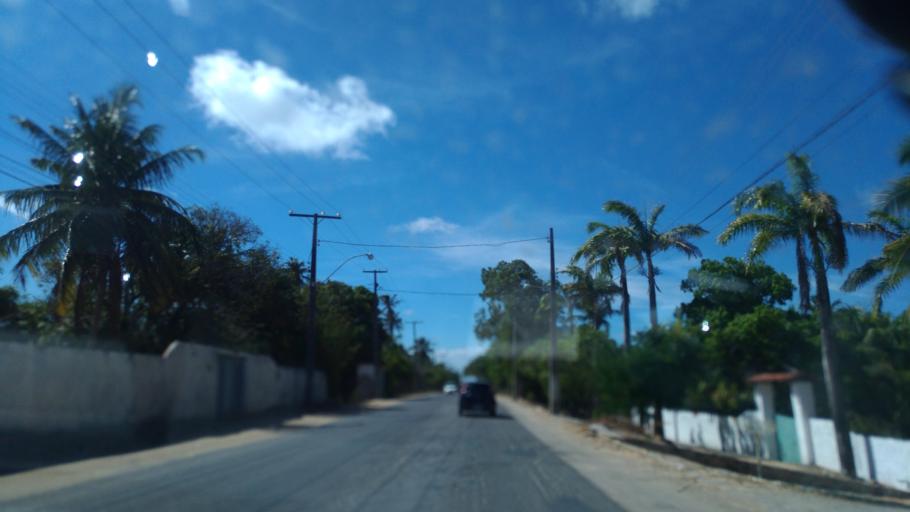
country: BR
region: Alagoas
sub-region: Marechal Deodoro
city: Marechal Deodoro
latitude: -9.7585
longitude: -35.8686
